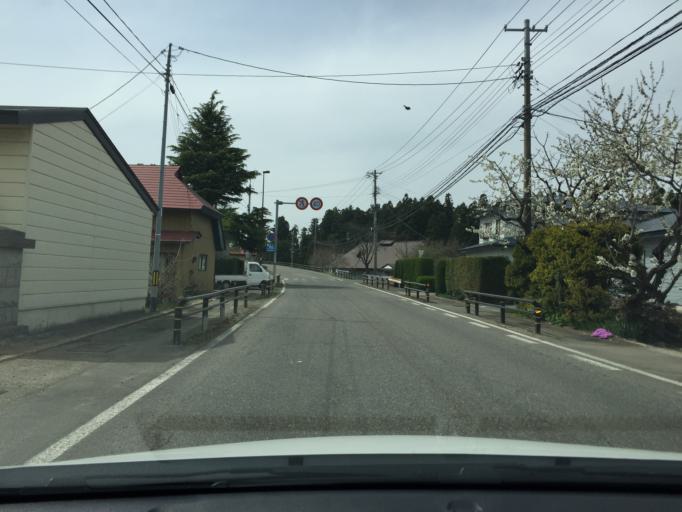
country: JP
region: Fukushima
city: Inawashiro
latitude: 37.5186
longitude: 140.1329
